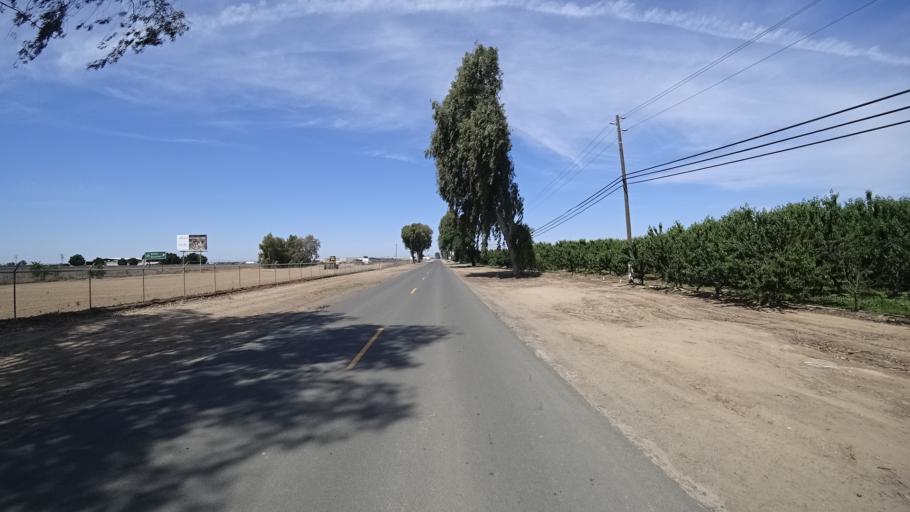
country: US
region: California
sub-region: Kings County
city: Home Garden
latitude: 36.3280
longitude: -119.5941
